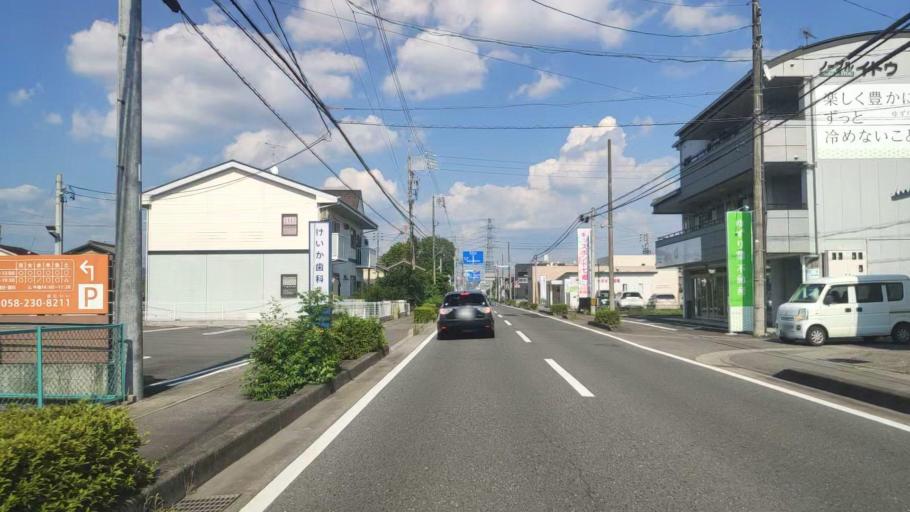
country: JP
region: Gifu
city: Gifu-shi
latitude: 35.4503
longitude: 136.7029
